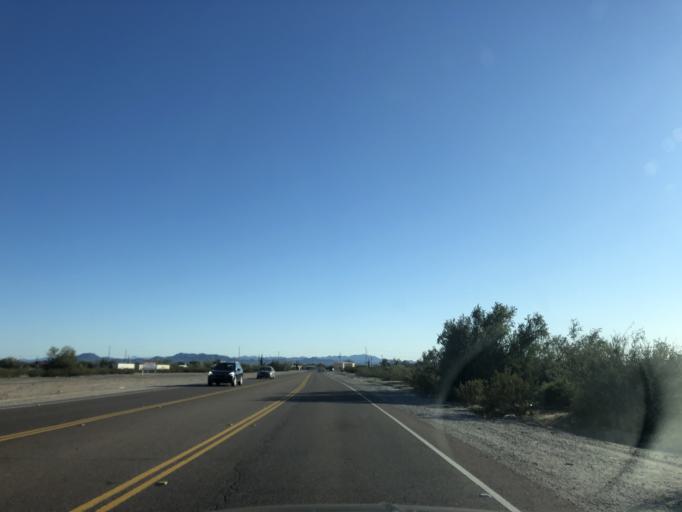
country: US
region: Arizona
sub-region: Maricopa County
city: Buckeye
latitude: 33.4318
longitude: -112.5867
